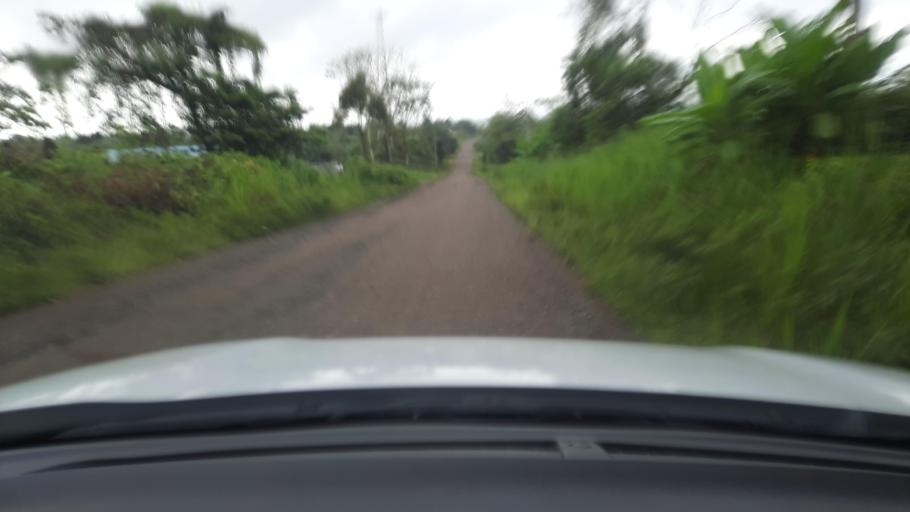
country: CR
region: Alajuela
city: San Jose
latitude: 11.0033
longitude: -85.3028
